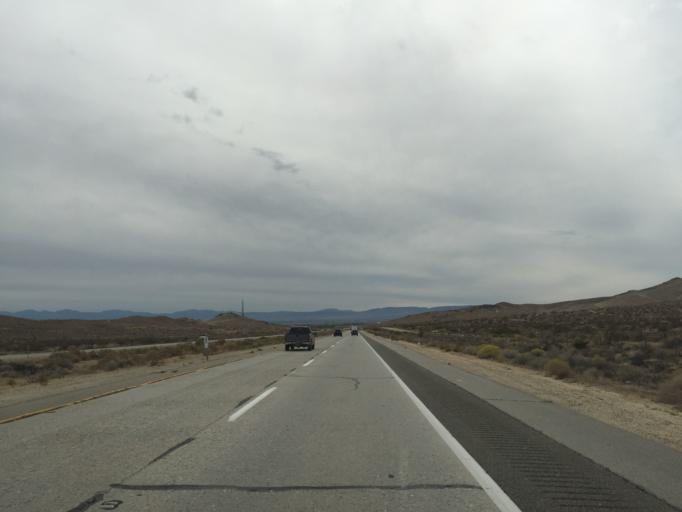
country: US
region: California
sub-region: Kern County
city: Rosamond
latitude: 34.8993
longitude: -118.1654
